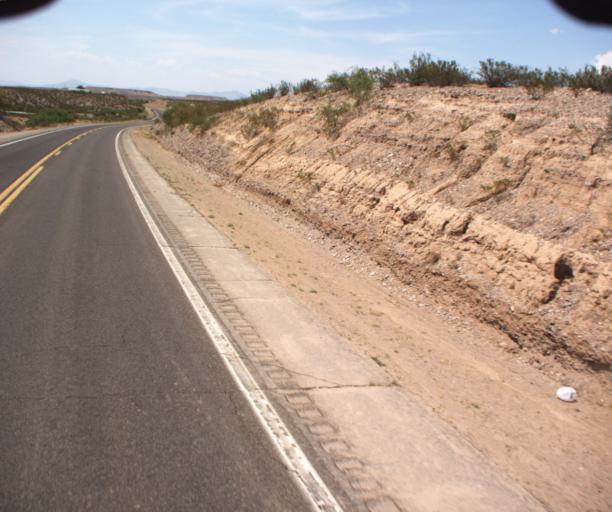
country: US
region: Arizona
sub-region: Greenlee County
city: Clifton
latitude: 32.8041
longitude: -109.1676
